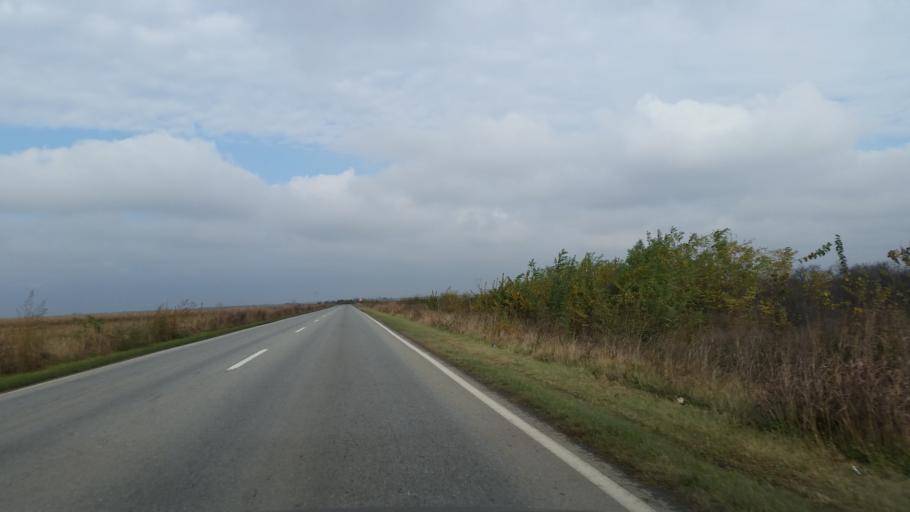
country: RS
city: Melenci
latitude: 45.4785
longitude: 20.3377
